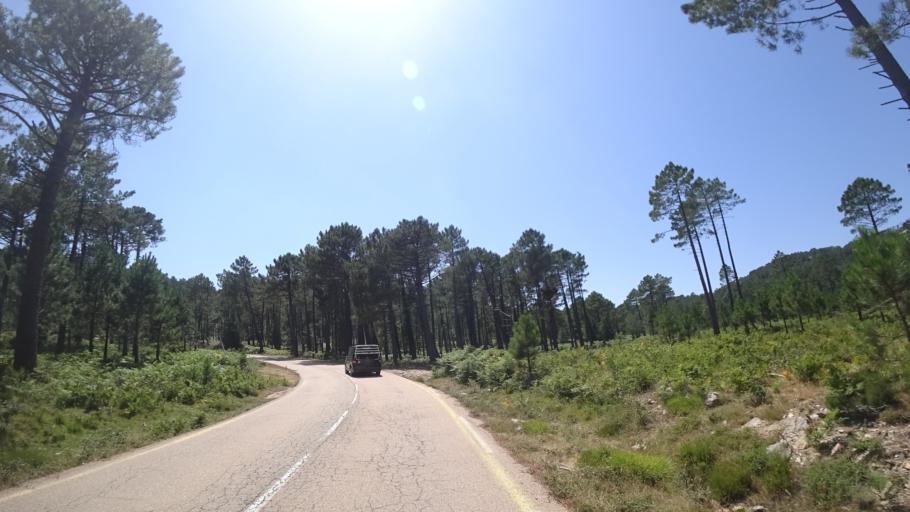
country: FR
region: Corsica
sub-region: Departement de la Corse-du-Sud
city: Zonza
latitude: 41.6865
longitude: 9.1960
